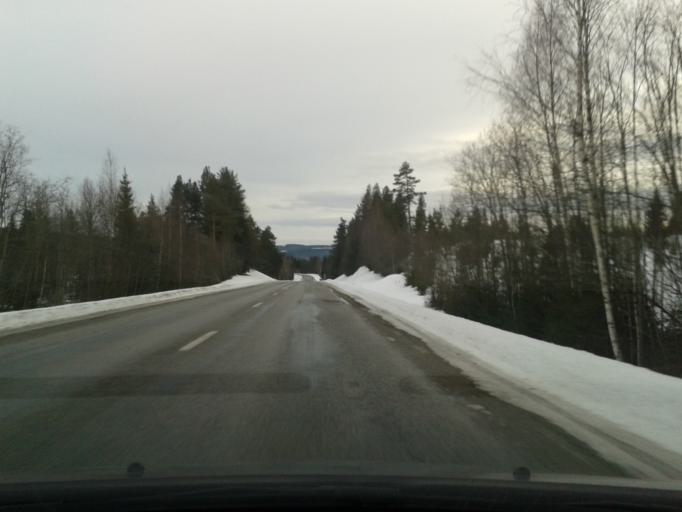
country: SE
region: Vaesternorrland
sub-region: Solleftea Kommun
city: As
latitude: 63.4891
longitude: 16.8637
